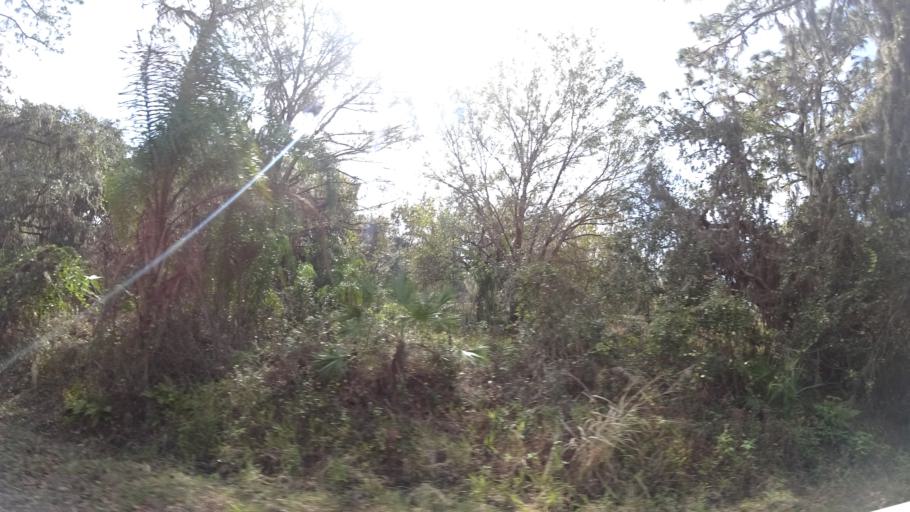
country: US
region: Florida
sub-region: Manatee County
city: Ellenton
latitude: 27.5762
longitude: -82.4403
